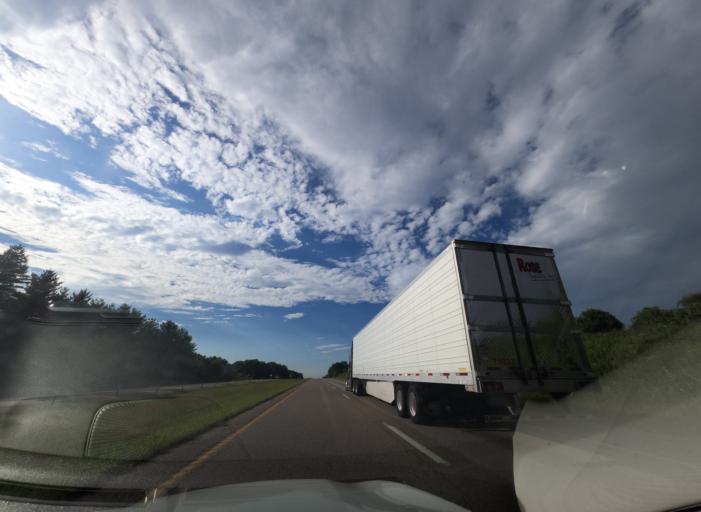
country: US
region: Missouri
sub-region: Jefferson County
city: Crystal City
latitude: 38.0442
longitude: -90.2652
